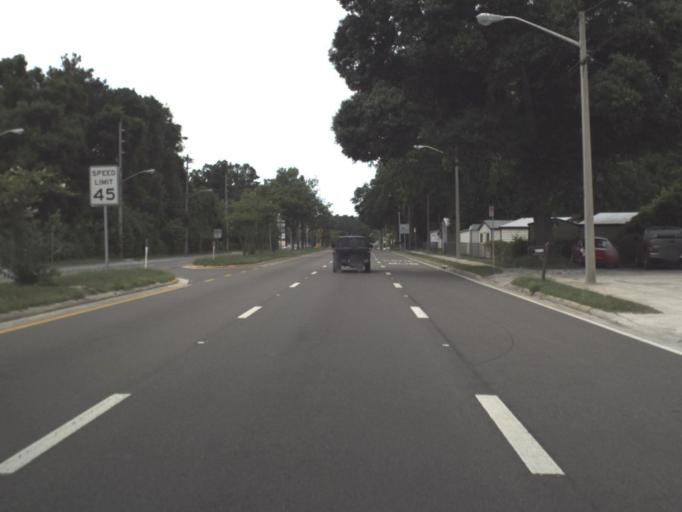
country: US
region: Florida
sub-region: Clay County
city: Bellair-Meadowbrook Terrace
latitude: 30.2369
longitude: -81.7403
